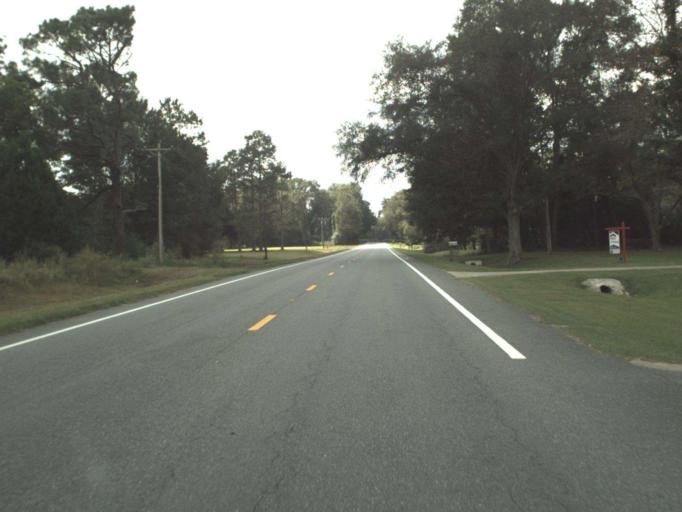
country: US
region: Florida
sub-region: Washington County
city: Chipley
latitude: 30.8051
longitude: -85.5147
